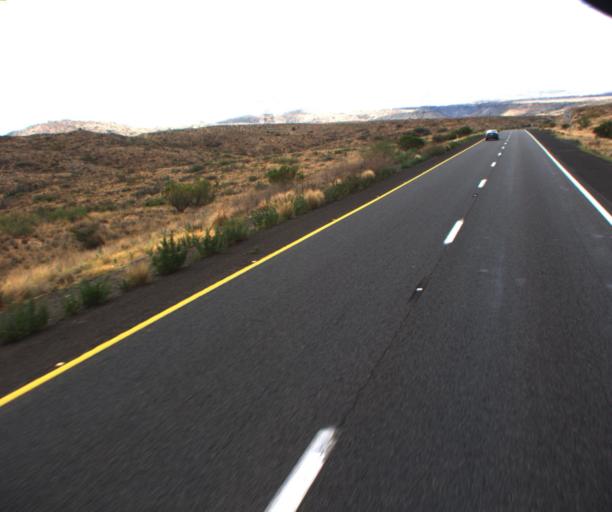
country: US
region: Arizona
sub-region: Yavapai County
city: Cordes Lakes
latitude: 34.2584
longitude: -112.1164
